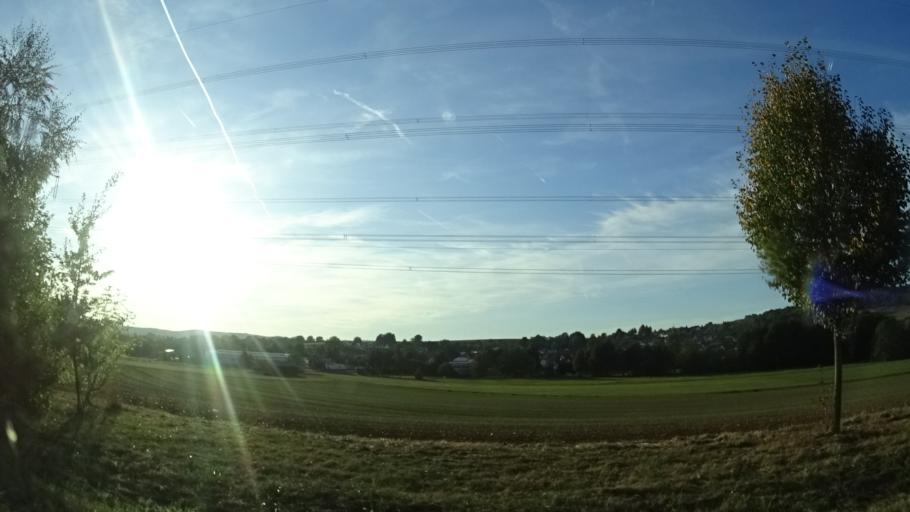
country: DE
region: Hesse
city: Hain-Grundau
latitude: 50.2398
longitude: 9.1484
